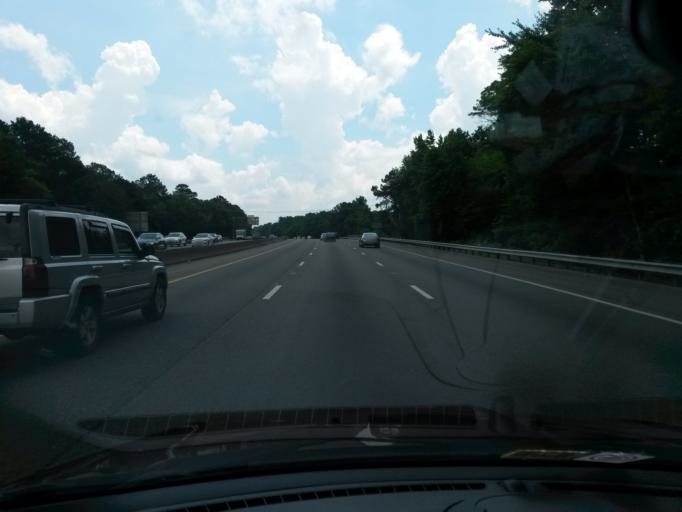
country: US
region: Virginia
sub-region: Chesterfield County
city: Bellwood
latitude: 37.3923
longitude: -77.4229
